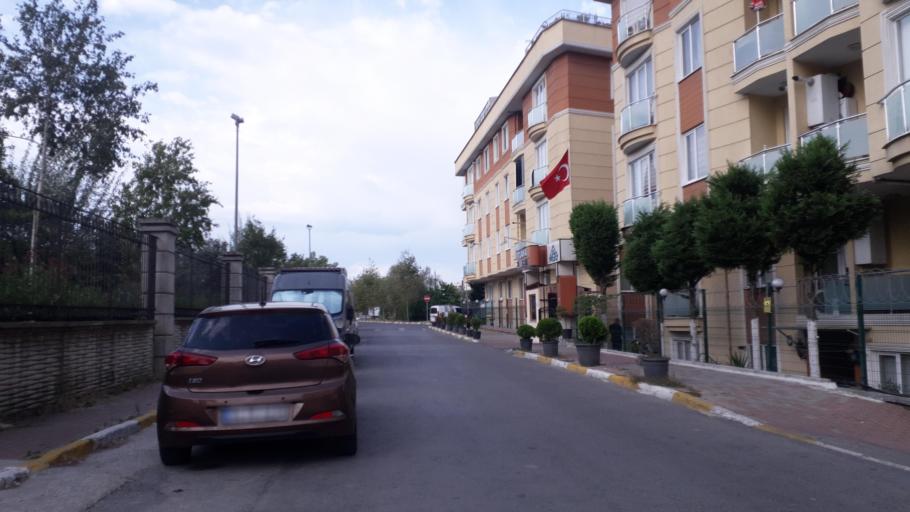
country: TR
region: Istanbul
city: Pendik
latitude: 40.9125
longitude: 29.3054
